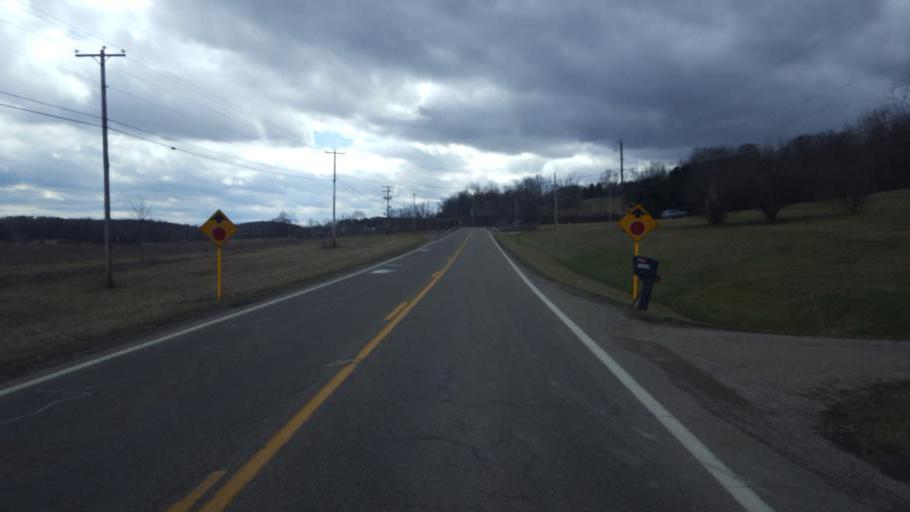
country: US
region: Ohio
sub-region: Muskingum County
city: Frazeysburg
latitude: 40.0669
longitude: -82.1579
